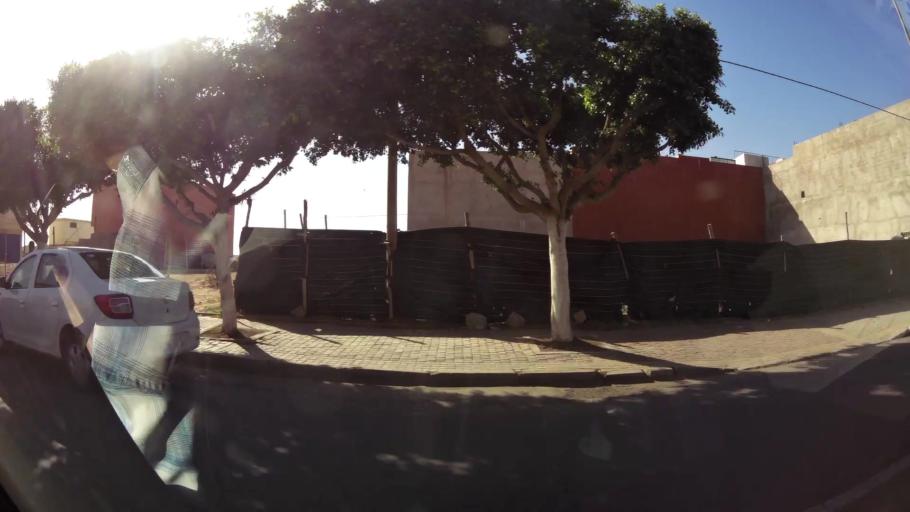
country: MA
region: Souss-Massa-Draa
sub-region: Inezgane-Ait Mellou
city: Inezgane
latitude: 30.3771
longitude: -9.5267
